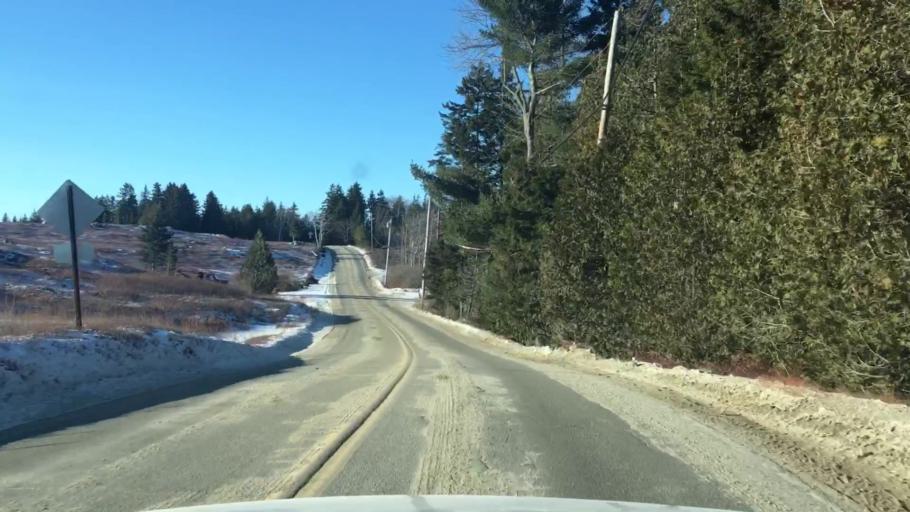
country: US
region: Maine
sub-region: Hancock County
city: Castine
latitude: 44.3647
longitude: -68.7501
